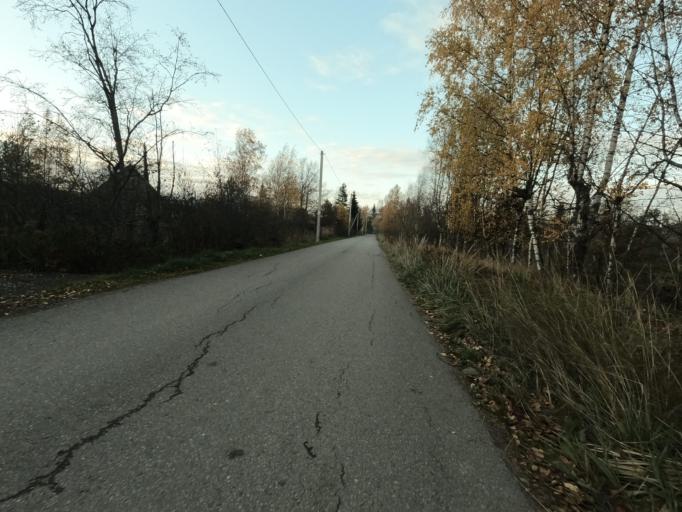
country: RU
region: Leningrad
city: Mga
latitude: 59.7787
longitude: 31.2048
